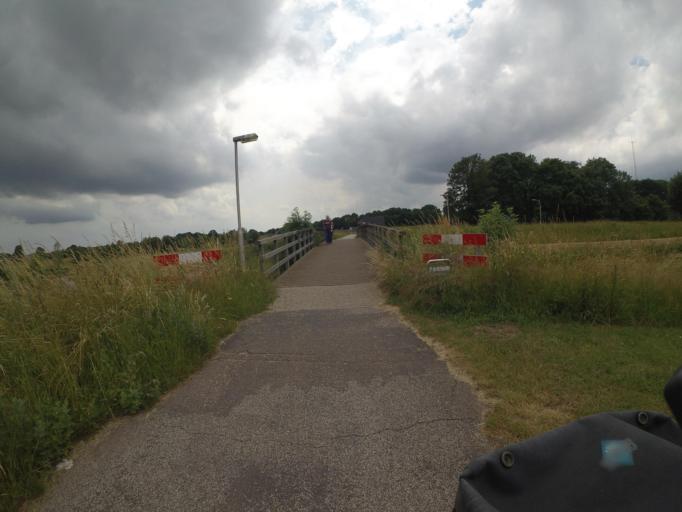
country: NL
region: Overijssel
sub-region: Gemeente Hardenberg
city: Hardenberg
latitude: 52.5717
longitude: 6.6121
